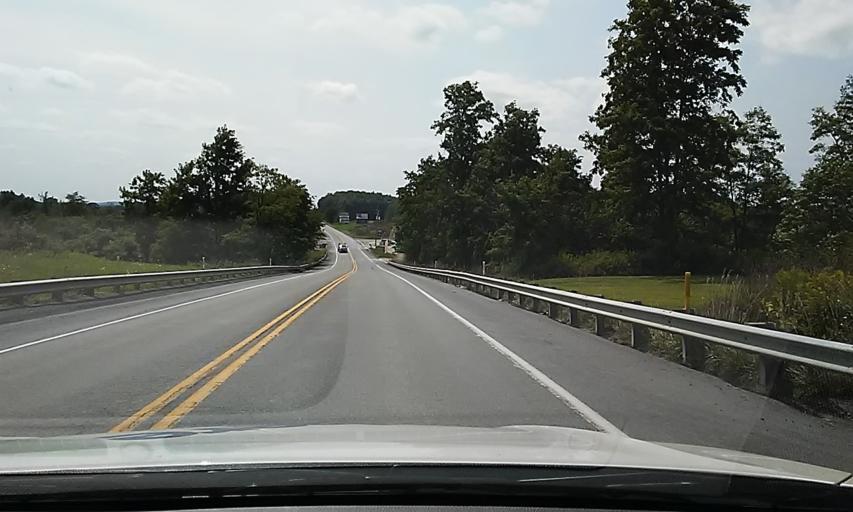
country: US
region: Pennsylvania
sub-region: Jefferson County
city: Punxsutawney
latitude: 40.9110
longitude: -78.9999
